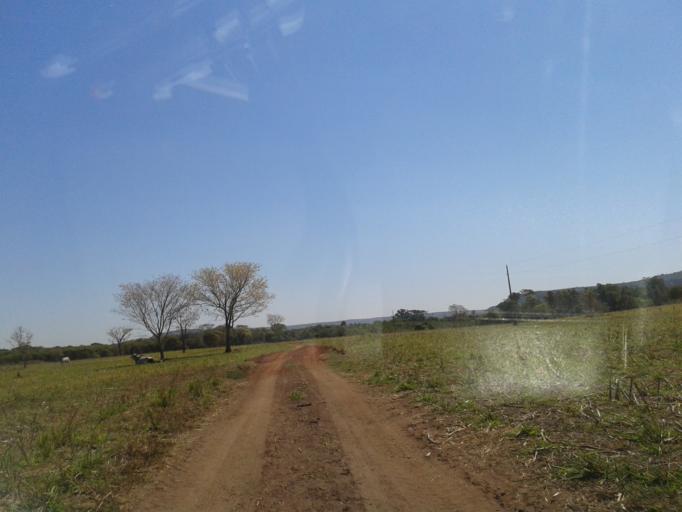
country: BR
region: Minas Gerais
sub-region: Santa Vitoria
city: Santa Vitoria
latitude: -19.0806
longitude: -50.0224
